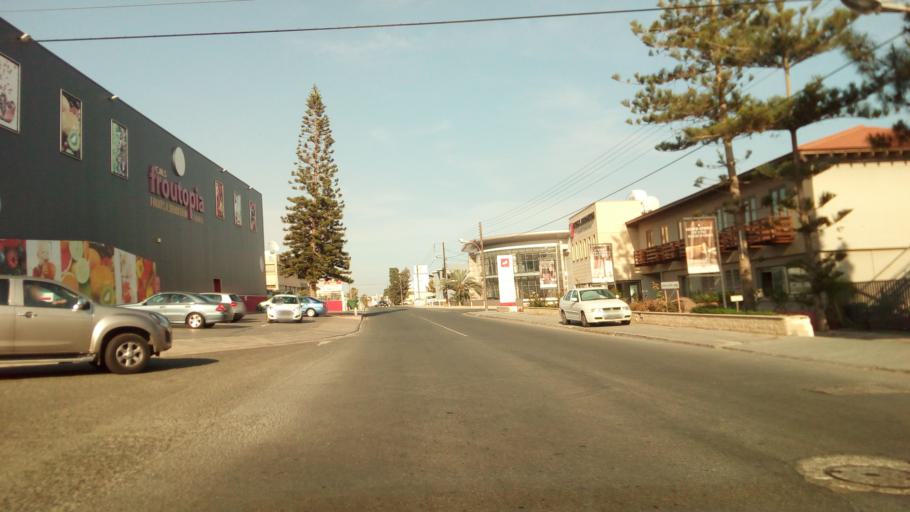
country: CY
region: Limassol
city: Limassol
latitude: 34.7047
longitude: 33.0656
